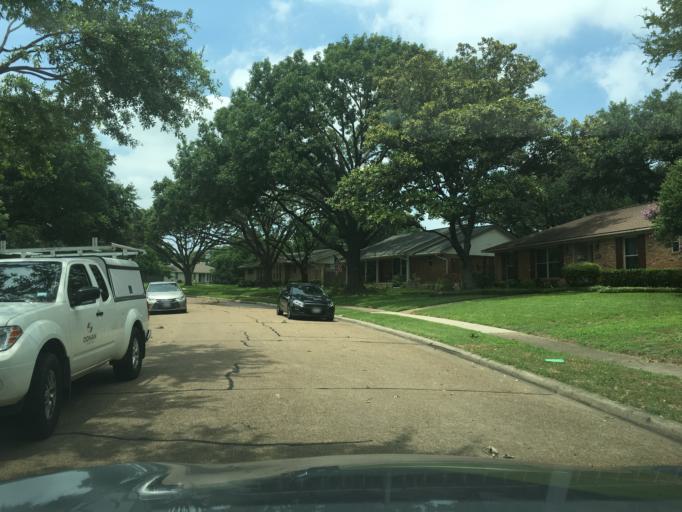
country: US
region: Texas
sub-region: Dallas County
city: Richardson
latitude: 32.9493
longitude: -96.7552
